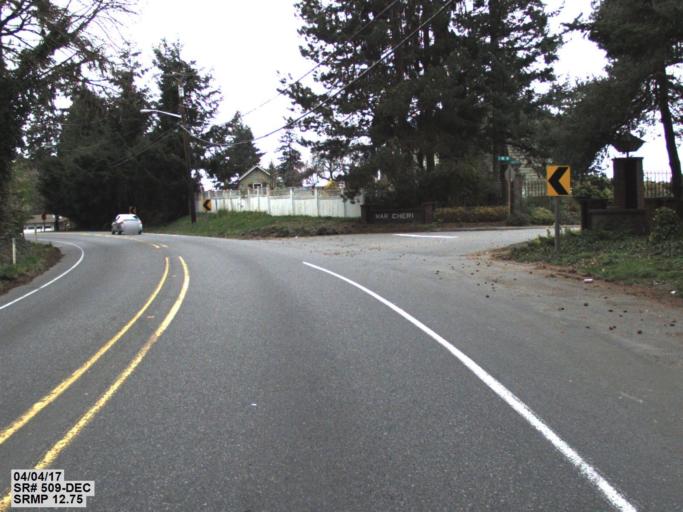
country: US
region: Washington
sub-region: King County
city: Federal Way
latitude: 47.3322
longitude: -122.3363
